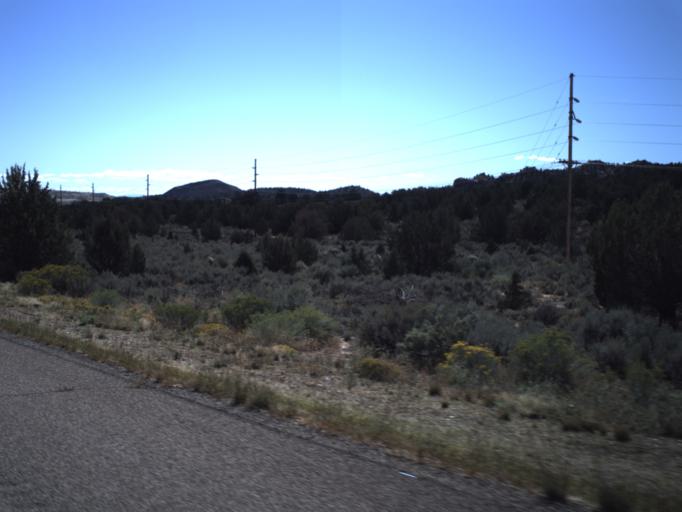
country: US
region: Utah
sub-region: Washington County
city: Ivins
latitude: 37.2725
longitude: -113.6431
